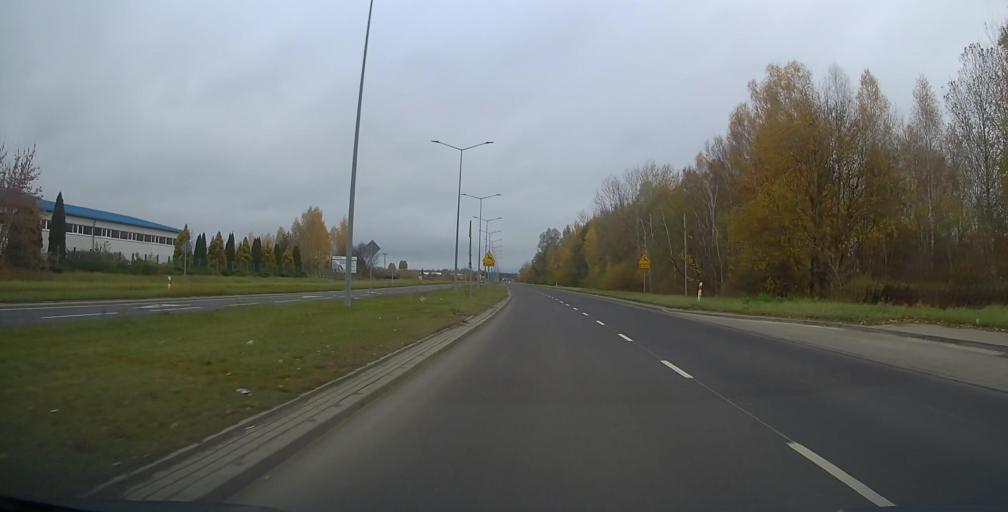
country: PL
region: Warmian-Masurian Voivodeship
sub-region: Powiat elcki
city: Elk
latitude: 53.8195
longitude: 22.3889
